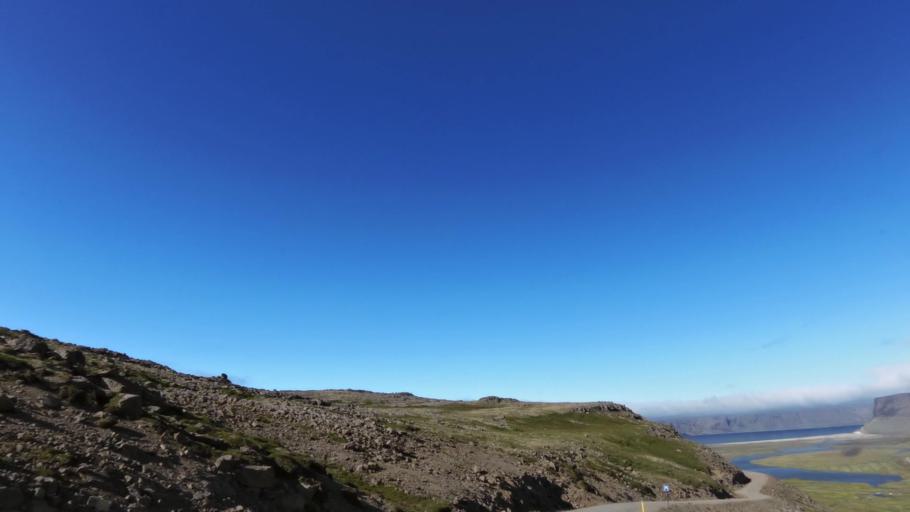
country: IS
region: West
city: Olafsvik
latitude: 65.5532
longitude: -24.2022
